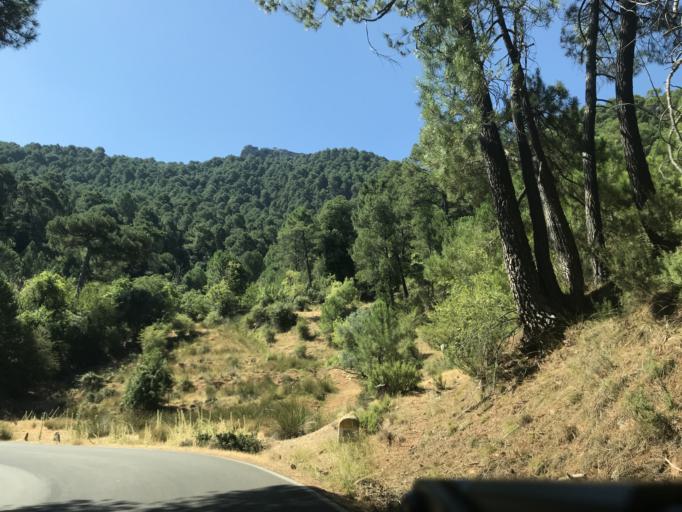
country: ES
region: Andalusia
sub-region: Provincia de Jaen
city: La Iruela
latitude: 37.9163
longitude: -2.9521
